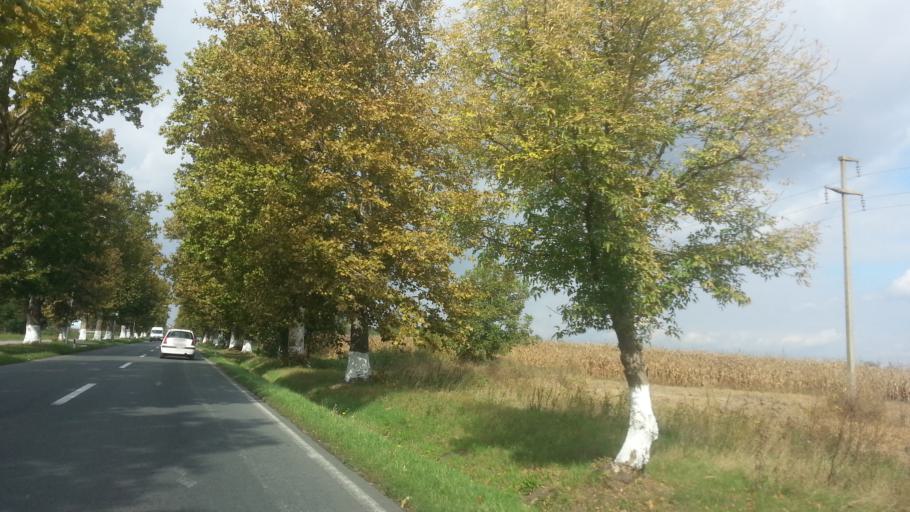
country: RS
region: Autonomna Pokrajina Vojvodina
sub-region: Sremski Okrug
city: Stara Pazova
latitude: 44.9721
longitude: 20.1750
